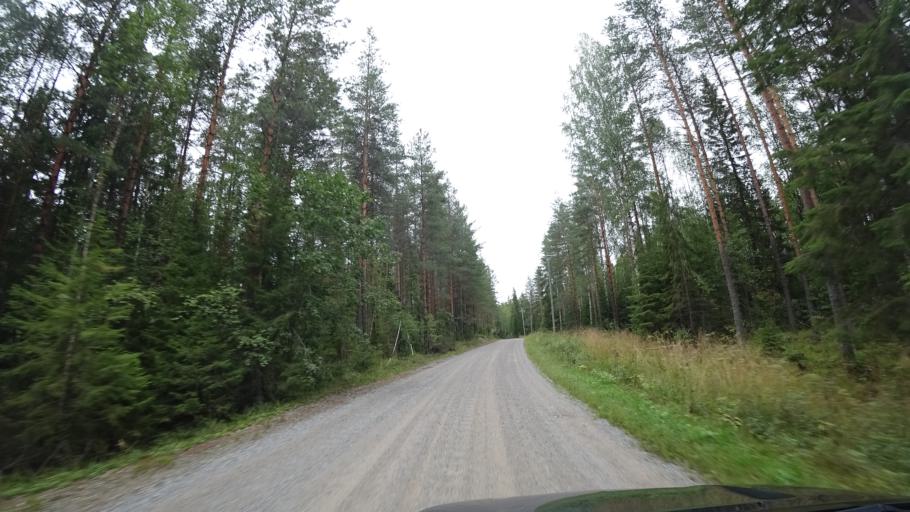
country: FI
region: Paijanne Tavastia
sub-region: Lahti
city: Auttoinen
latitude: 61.2189
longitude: 25.1387
